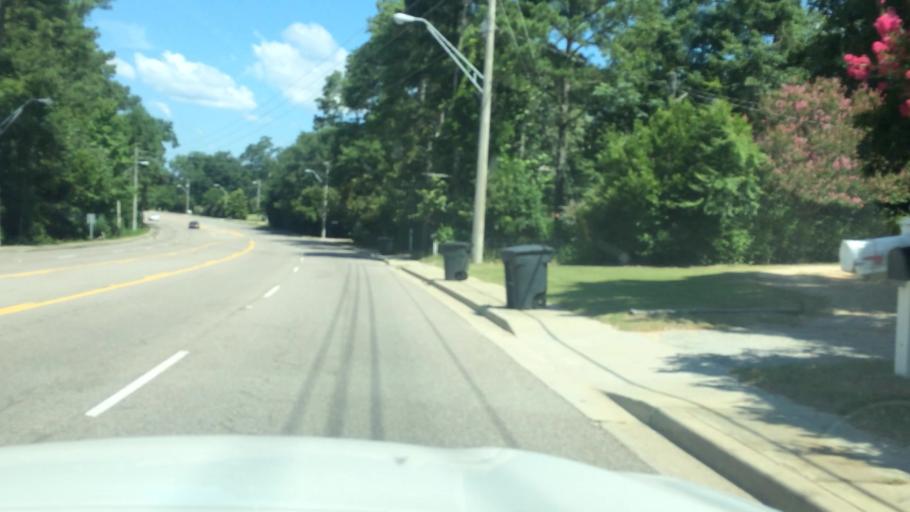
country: US
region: South Carolina
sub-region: Aiken County
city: North Augusta
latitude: 33.5281
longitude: -81.9801
